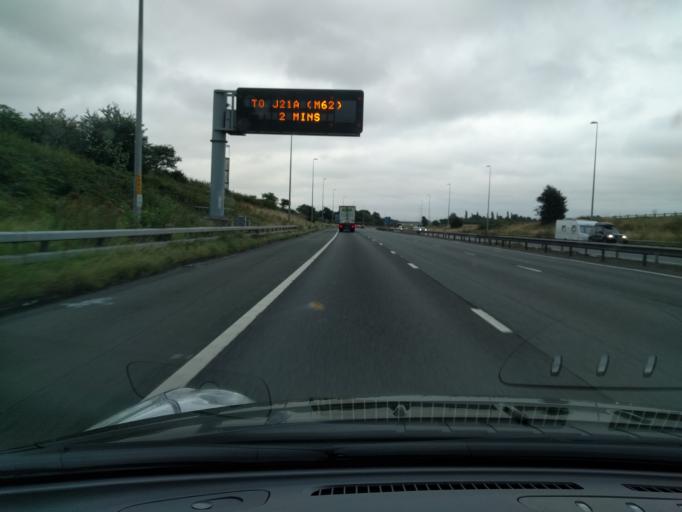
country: GB
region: England
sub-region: St. Helens
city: Newton-le-Willows
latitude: 53.4492
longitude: -2.5956
